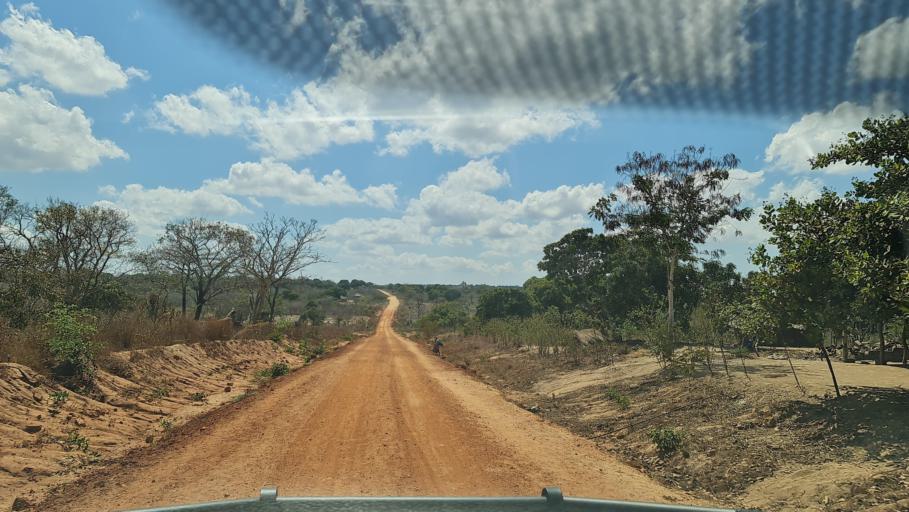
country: MZ
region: Nampula
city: Nacala
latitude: -14.1757
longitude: 40.2321
